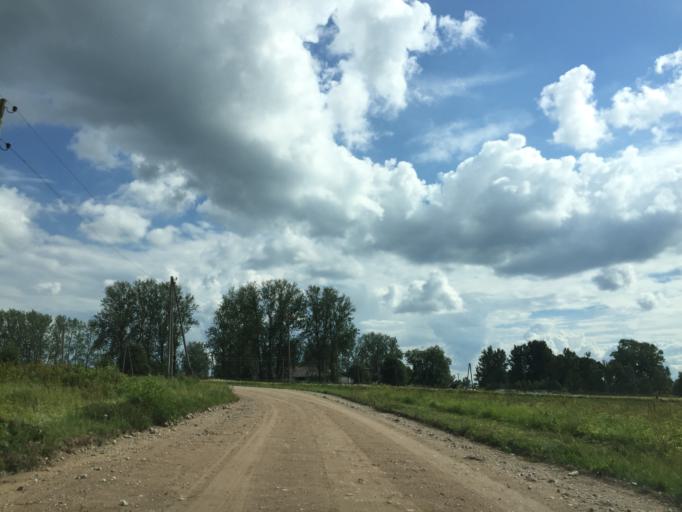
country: LV
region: Ligatne
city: Ligatne
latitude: 57.2092
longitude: 24.9591
